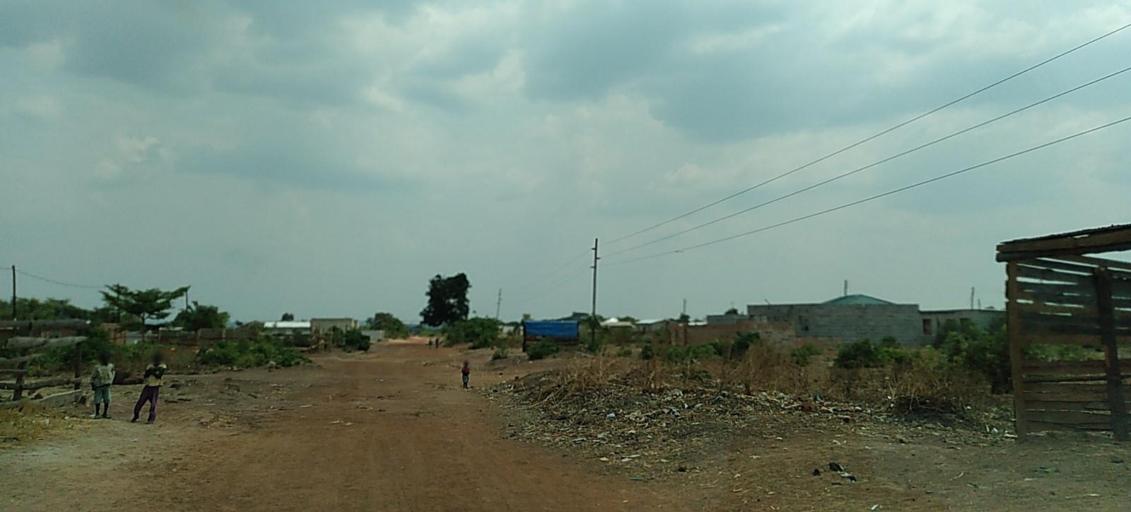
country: ZM
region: Copperbelt
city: Kalulushi
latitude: -12.8661
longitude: 28.0780
